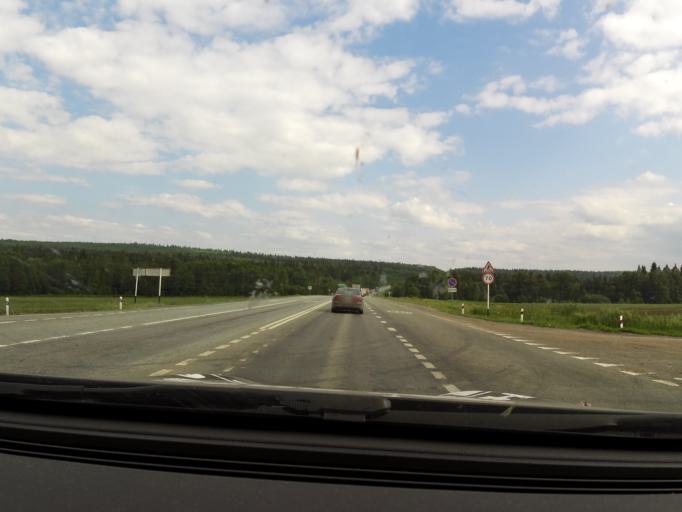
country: RU
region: Sverdlovsk
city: Bilimbay
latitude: 56.8485
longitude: 59.8132
